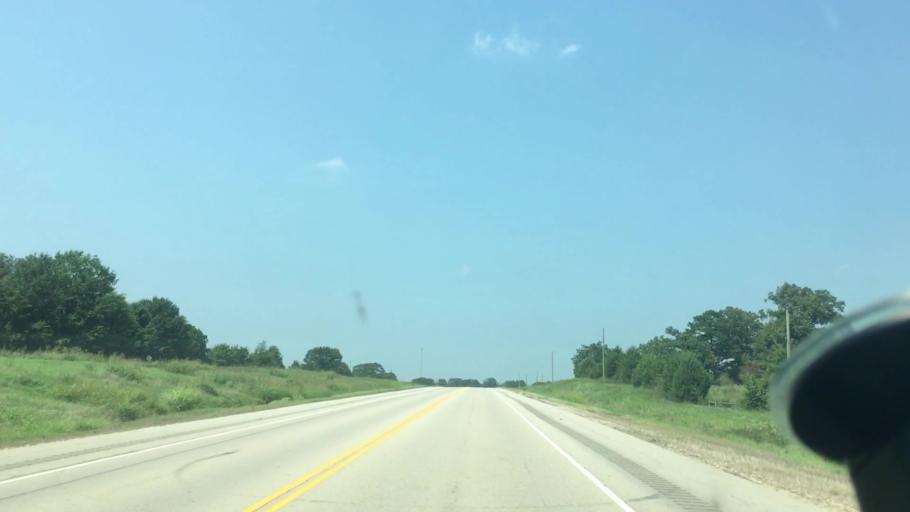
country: US
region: Oklahoma
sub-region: Atoka County
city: Atoka
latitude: 34.2882
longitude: -95.9630
